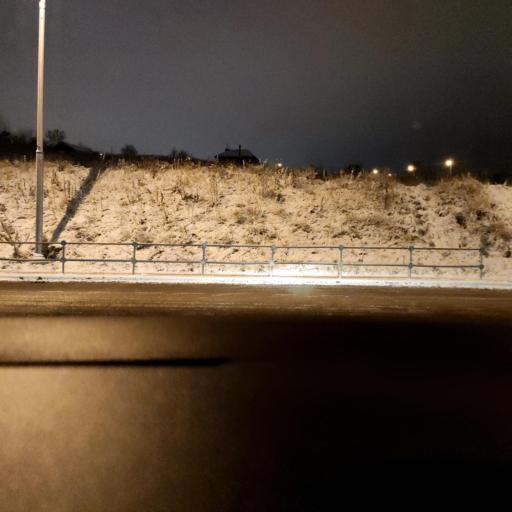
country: RU
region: Moskovskaya
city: Pavshino
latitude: 55.8621
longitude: 37.3720
